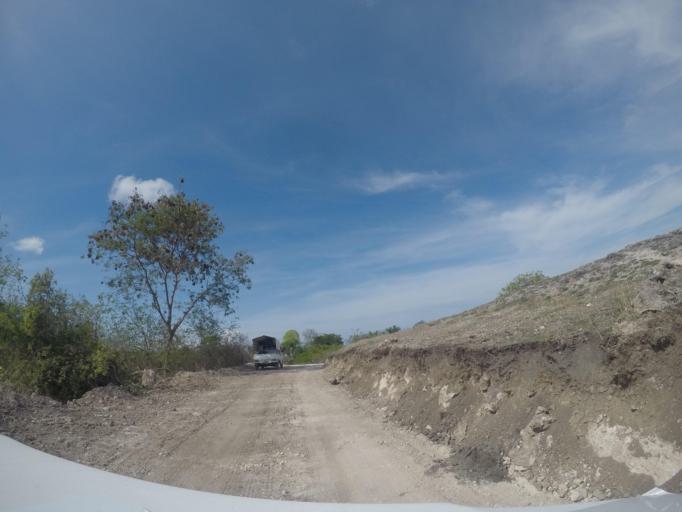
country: TL
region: Baucau
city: Baucau
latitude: -8.4708
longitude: 126.4732
